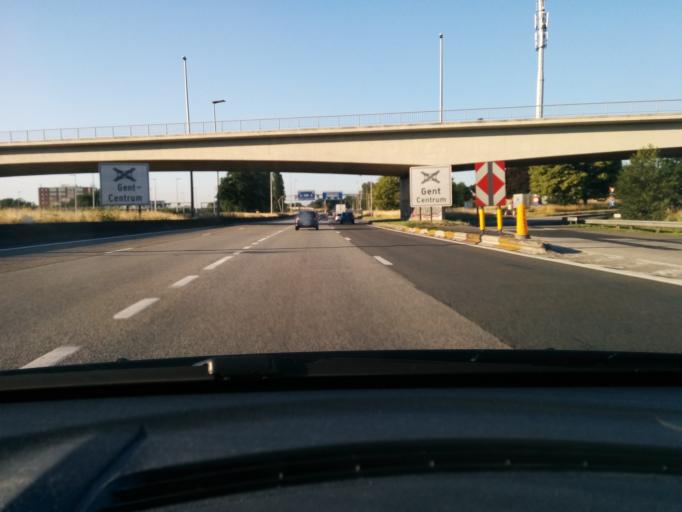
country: BE
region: Flanders
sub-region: Provincie Oost-Vlaanderen
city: Ledeberg
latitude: 51.0210
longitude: 3.7336
